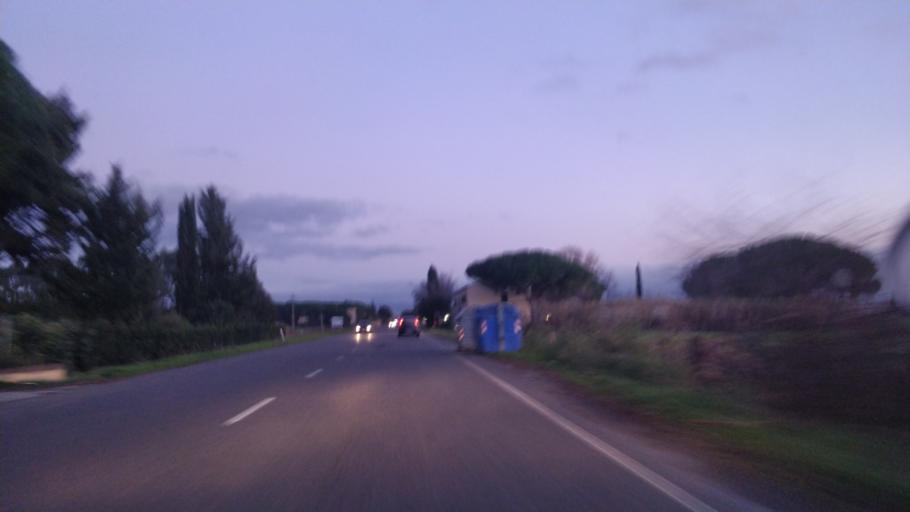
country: IT
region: Tuscany
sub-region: Provincia di Livorno
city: Vada
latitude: 43.3415
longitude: 10.4779
